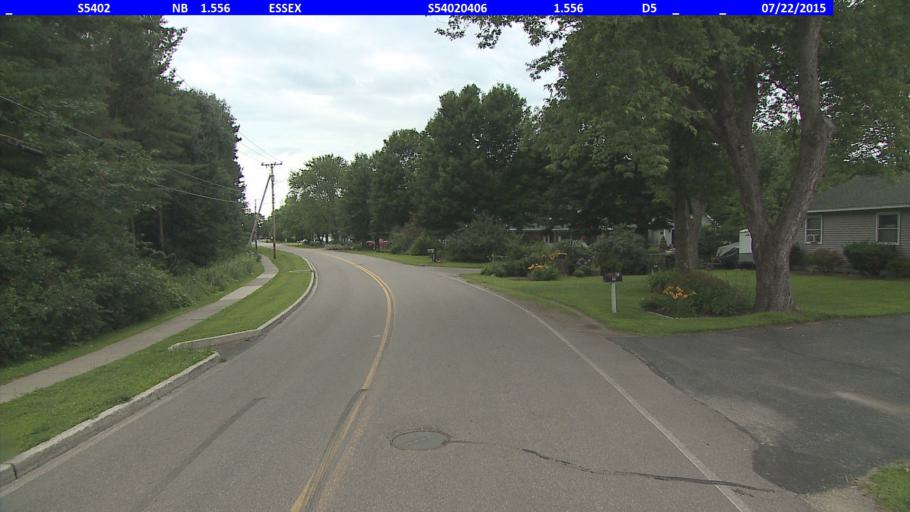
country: US
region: Vermont
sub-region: Chittenden County
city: Jericho
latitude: 44.5005
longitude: -73.0491
